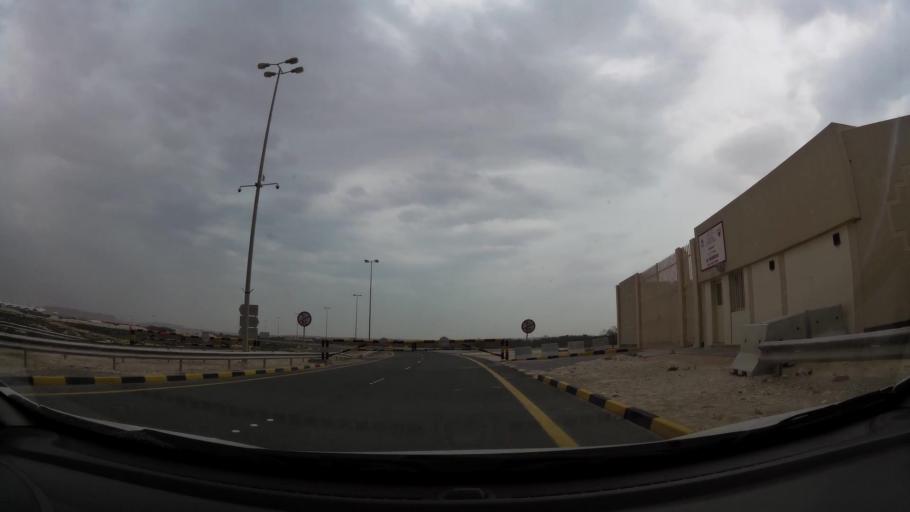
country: BH
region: Central Governorate
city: Dar Kulayb
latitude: 26.0246
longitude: 50.4934
